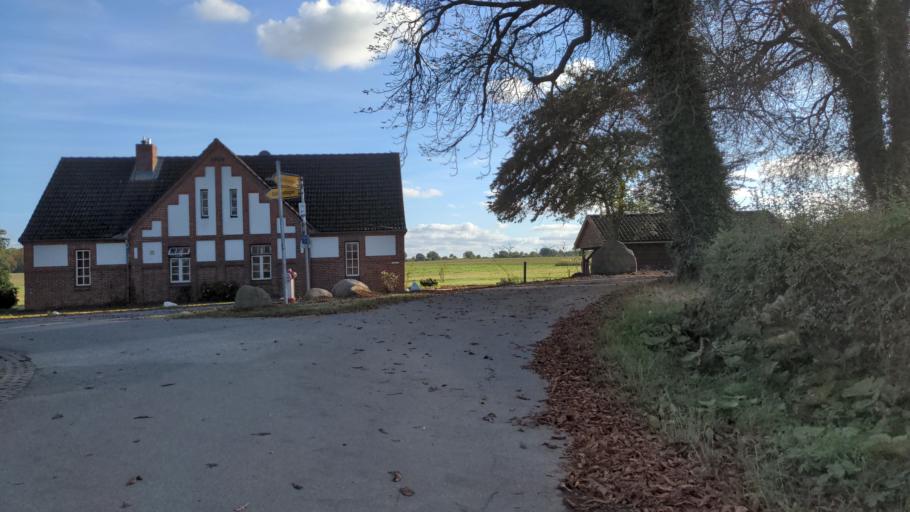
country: DE
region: Schleswig-Holstein
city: Manhagen
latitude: 54.1845
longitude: 10.9103
